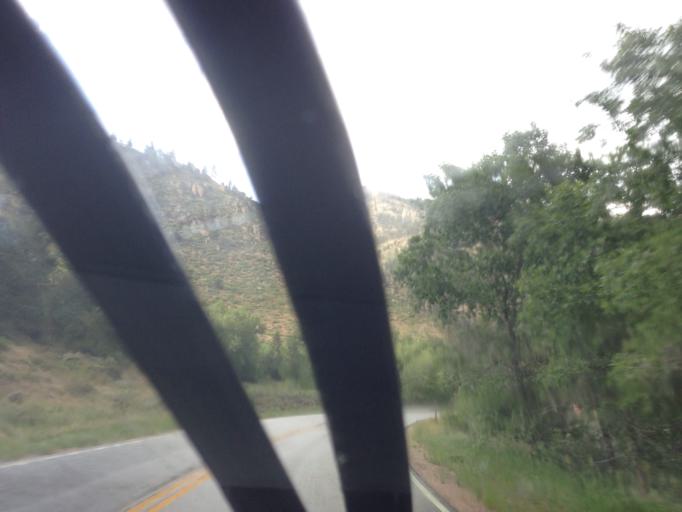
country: US
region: Colorado
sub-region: Larimer County
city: Estes Park
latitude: 40.6980
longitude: -105.6764
